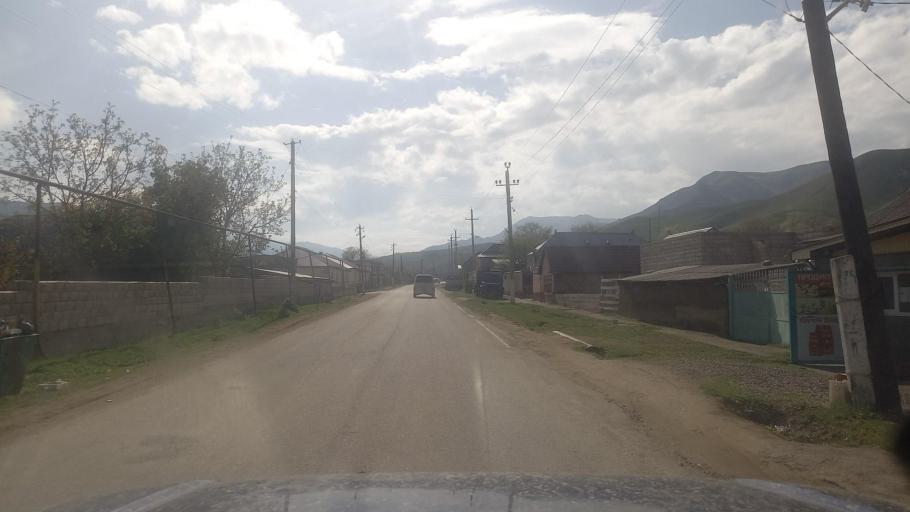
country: RU
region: Kabardino-Balkariya
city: Kamennomostskoye
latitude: 43.7302
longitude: 42.9403
